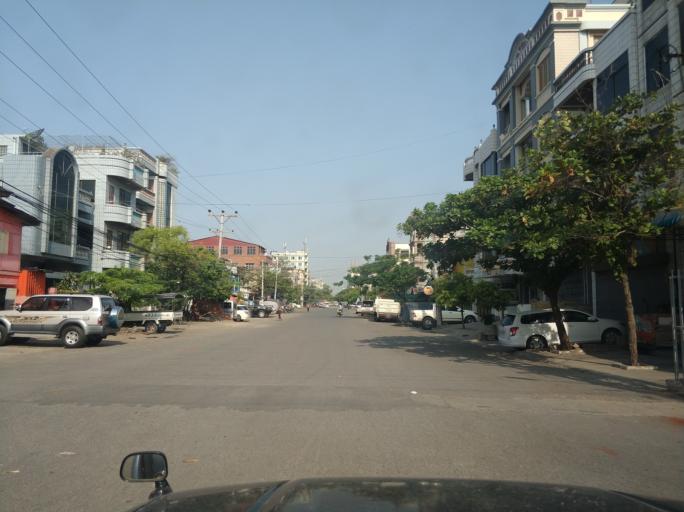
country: MM
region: Mandalay
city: Mandalay
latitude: 21.9704
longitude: 96.0929
